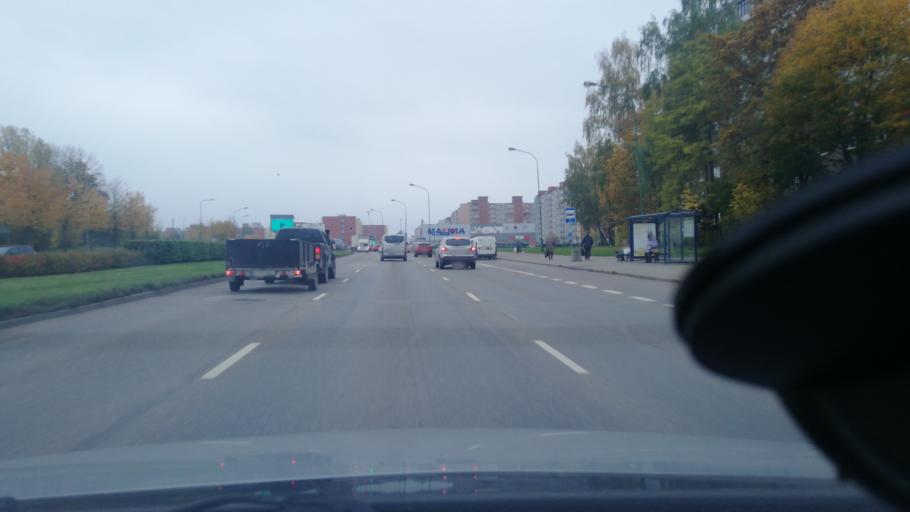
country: LT
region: Klaipedos apskritis
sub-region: Klaipeda
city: Klaipeda
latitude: 55.6792
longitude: 21.1876
